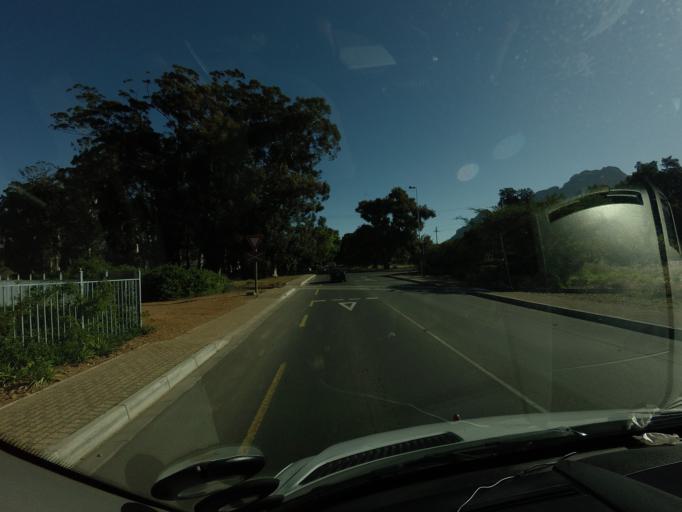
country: ZA
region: Western Cape
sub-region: Cape Winelands District Municipality
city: Paarl
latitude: -33.8653
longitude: 18.9787
